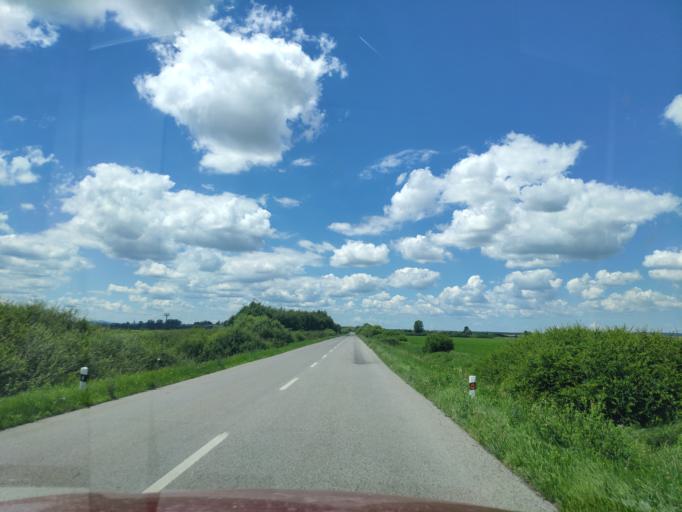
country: HU
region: Borsod-Abauj-Zemplen
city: Ozd
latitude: 48.3095
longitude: 20.2635
